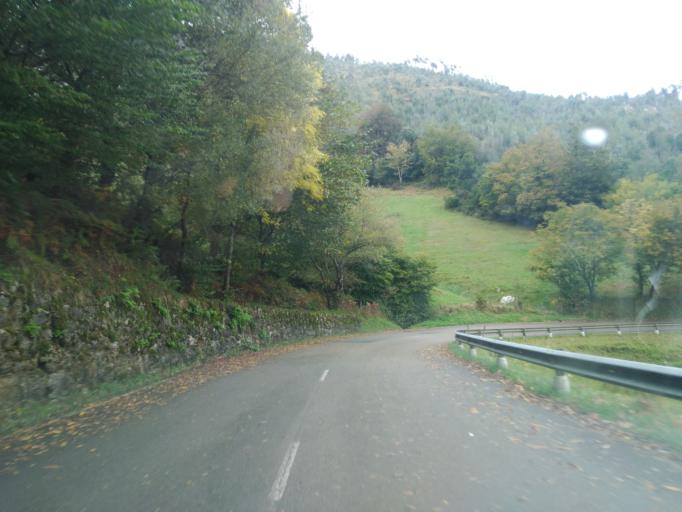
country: ES
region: Cantabria
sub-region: Provincia de Cantabria
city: Puente Viesgo
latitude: 43.2930
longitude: -3.9715
